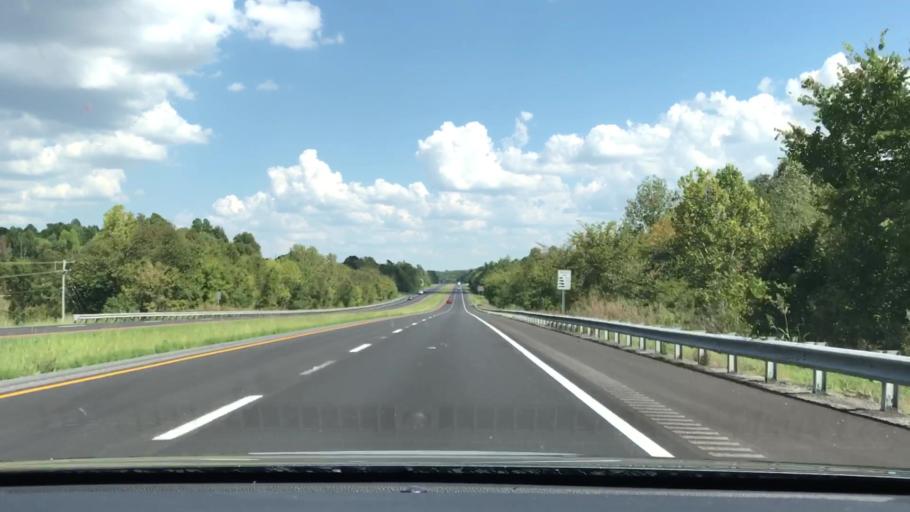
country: US
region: Kentucky
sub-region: Lyon County
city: Eddyville
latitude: 37.0871
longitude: -88.0616
